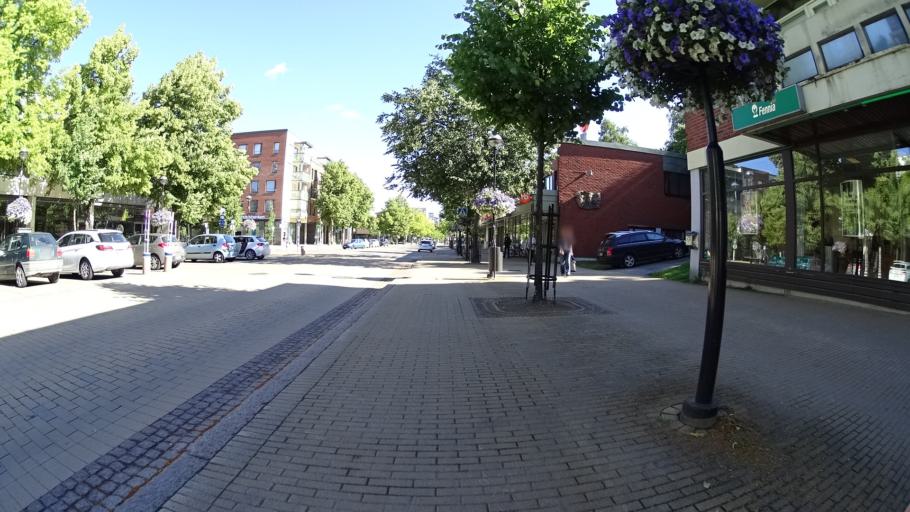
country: FI
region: Uusimaa
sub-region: Helsinki
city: Kerava
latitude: 60.4037
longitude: 25.1017
